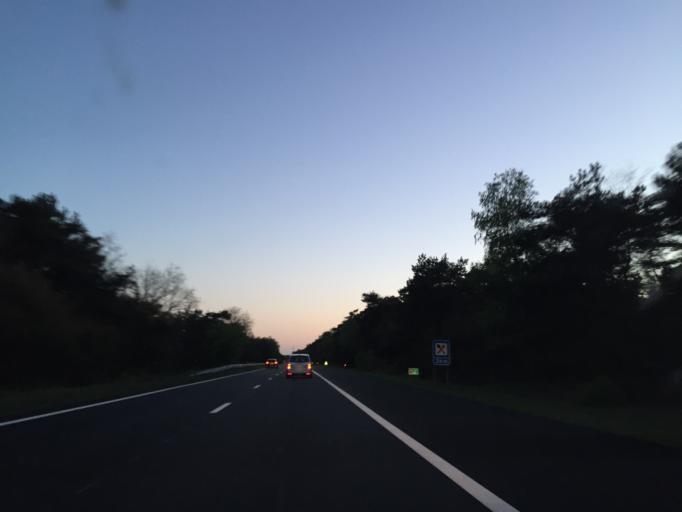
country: NL
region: Gelderland
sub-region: Gemeente Oldebroek
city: Oldebroek
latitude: 52.4294
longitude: 5.9343
